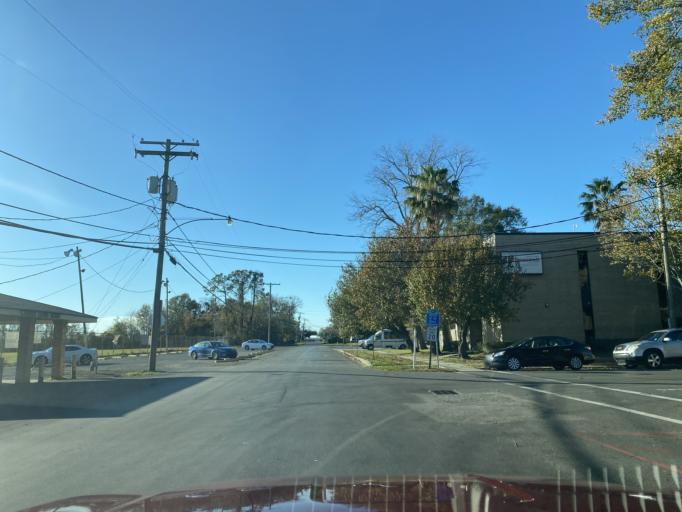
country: US
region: Louisiana
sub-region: Jefferson Parish
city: Kenner
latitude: 29.9897
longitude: -90.2431
